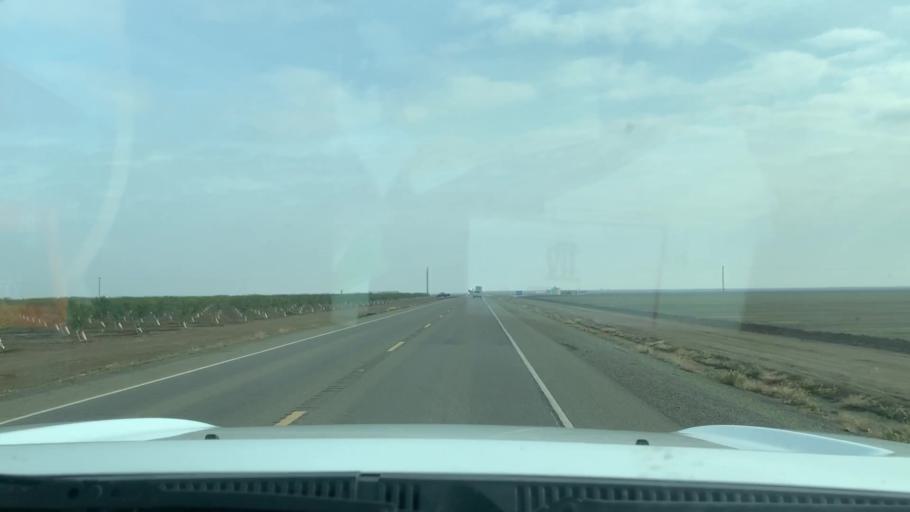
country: US
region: California
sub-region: Kings County
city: Lemoore Station
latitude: 36.2554
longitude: -119.9981
